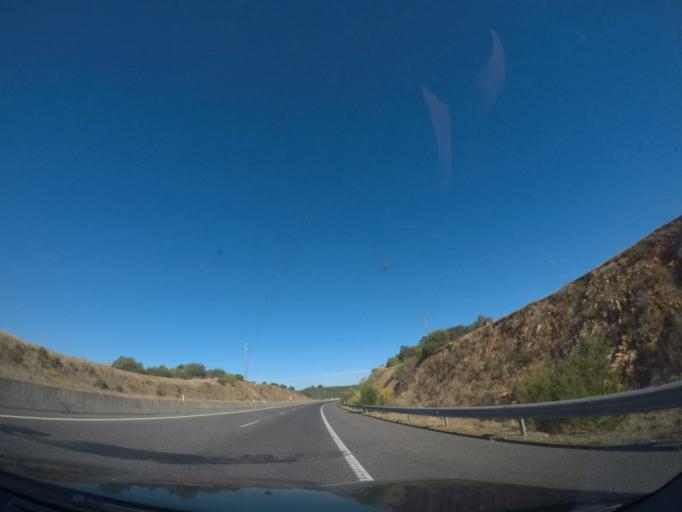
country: PT
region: Faro
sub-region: Portimao
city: Alvor
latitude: 37.1760
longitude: -8.5733
